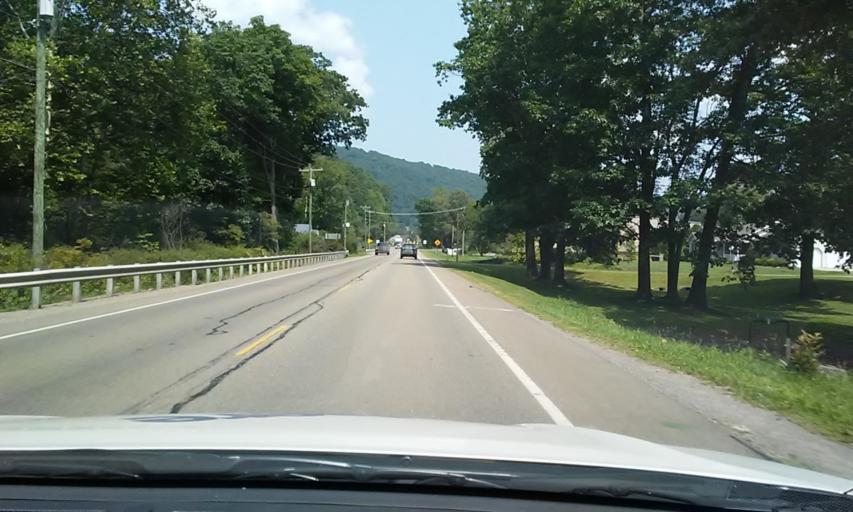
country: US
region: Pennsylvania
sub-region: Cameron County
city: Emporium
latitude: 41.5069
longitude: -78.2523
